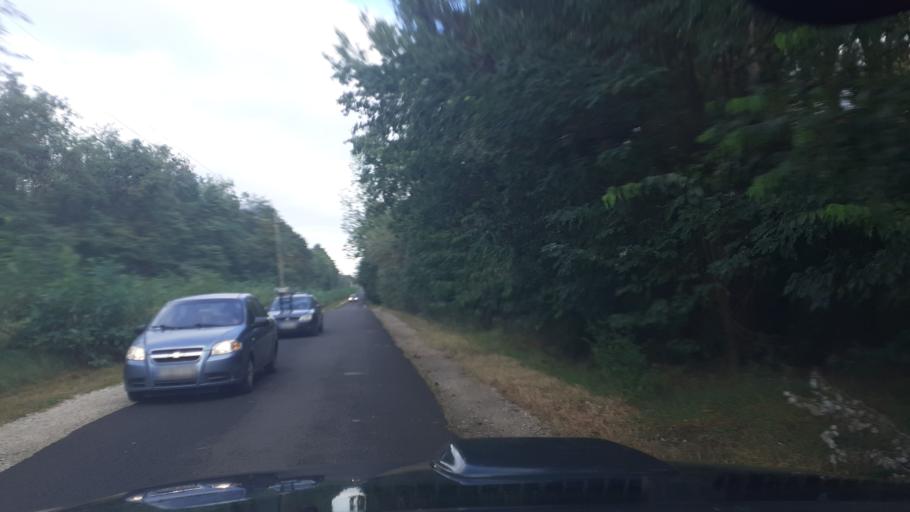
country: HU
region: Fejer
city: Baracs
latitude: 46.9413
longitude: 18.8650
